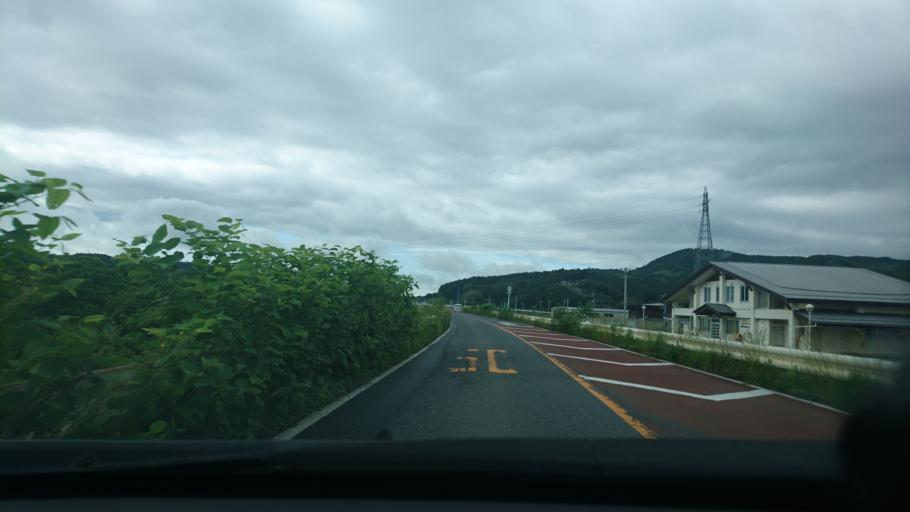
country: JP
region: Miyagi
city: Wakuya
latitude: 38.6163
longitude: 141.2988
